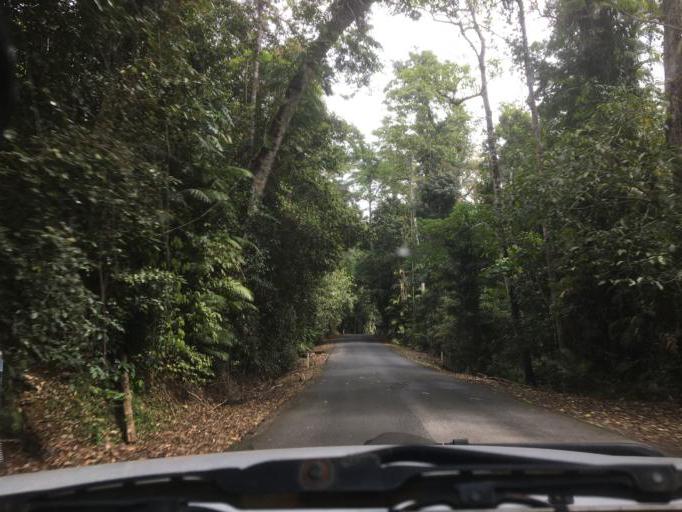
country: AU
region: Queensland
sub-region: Tablelands
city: Tolga
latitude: -17.2811
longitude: 145.6205
